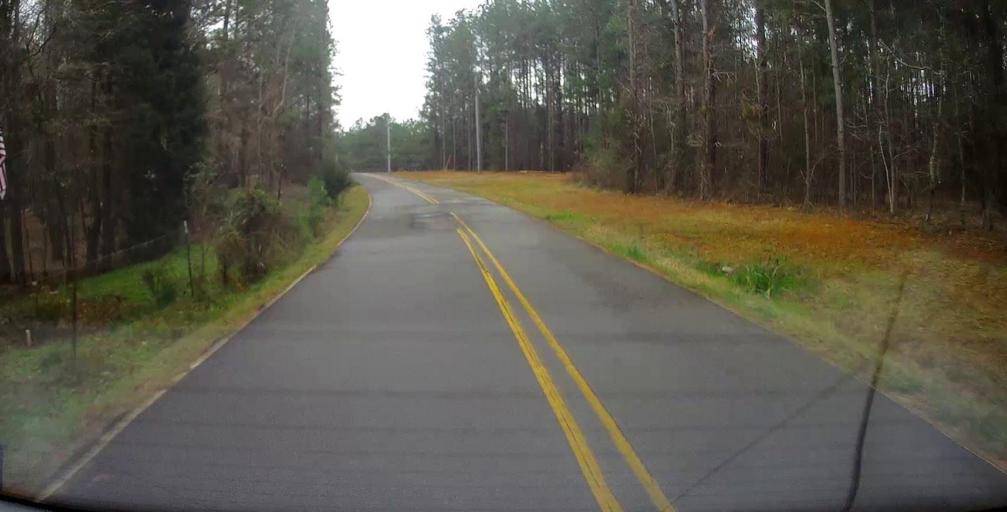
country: US
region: Georgia
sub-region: Monroe County
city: Forsyth
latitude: 33.0104
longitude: -83.8211
